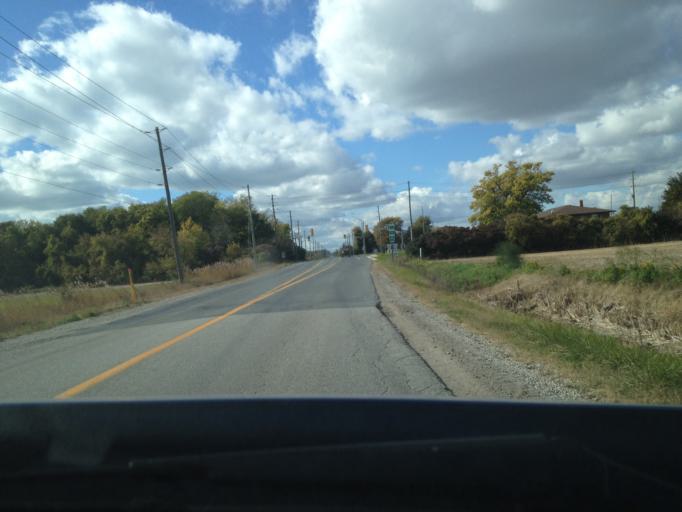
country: CA
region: Ontario
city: Amherstburg
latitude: 42.0330
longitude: -82.5786
